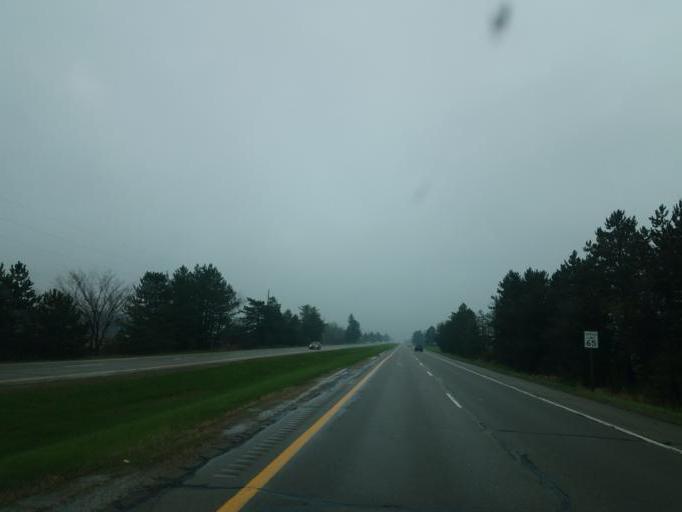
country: US
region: Michigan
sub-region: Clinton County
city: Saint Johns
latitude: 43.0722
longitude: -84.5639
